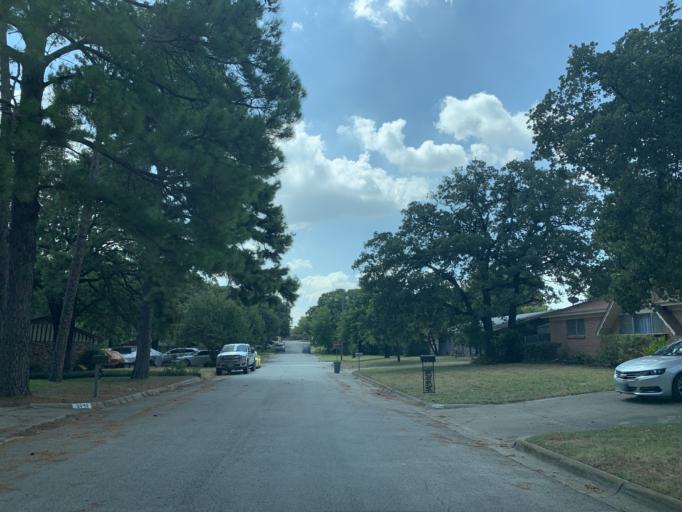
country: US
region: Texas
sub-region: Tarrant County
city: Azle
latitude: 32.8772
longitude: -97.5299
